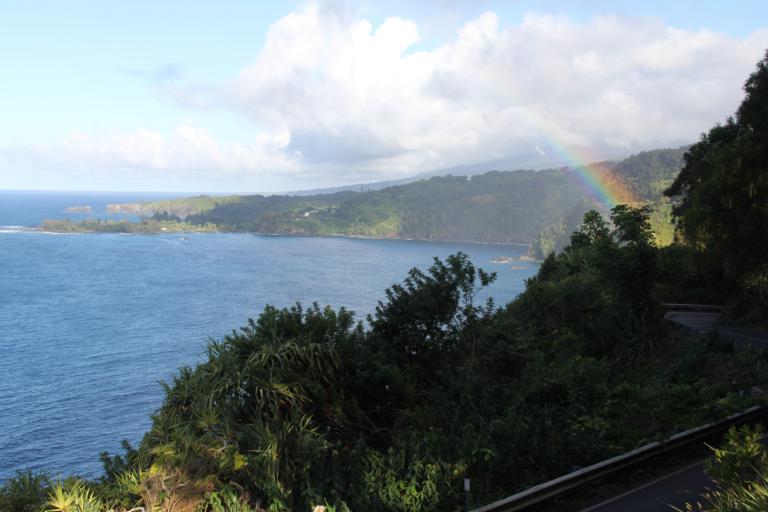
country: US
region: Hawaii
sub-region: Maui County
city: Wailua
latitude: 20.8712
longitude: -156.1686
